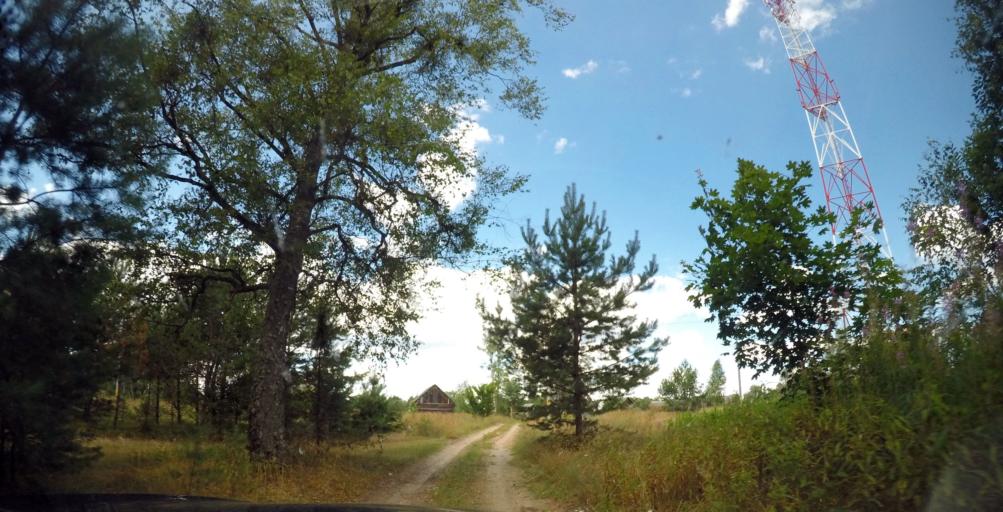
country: BY
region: Grodnenskaya
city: Skidal'
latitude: 53.8190
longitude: 24.2477
